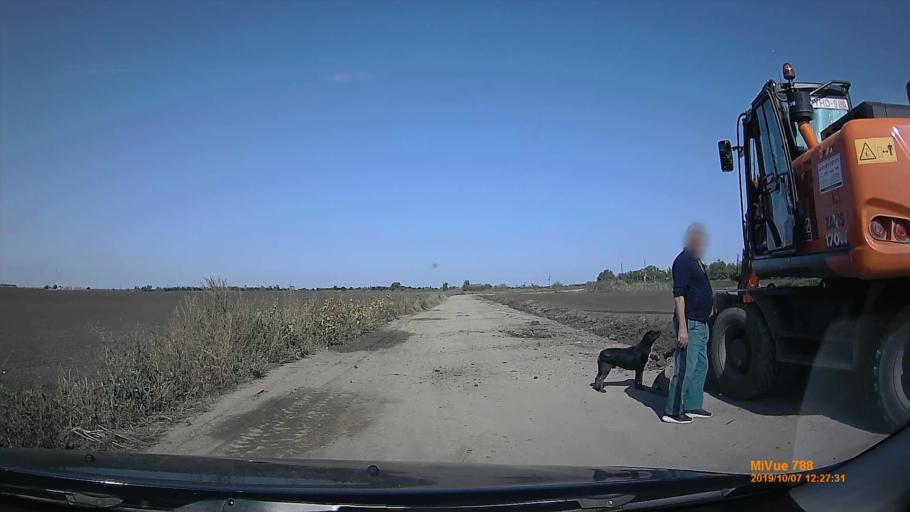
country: HU
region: Jasz-Nagykun-Szolnok
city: Kunszentmarton
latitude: 46.8698
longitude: 20.2731
